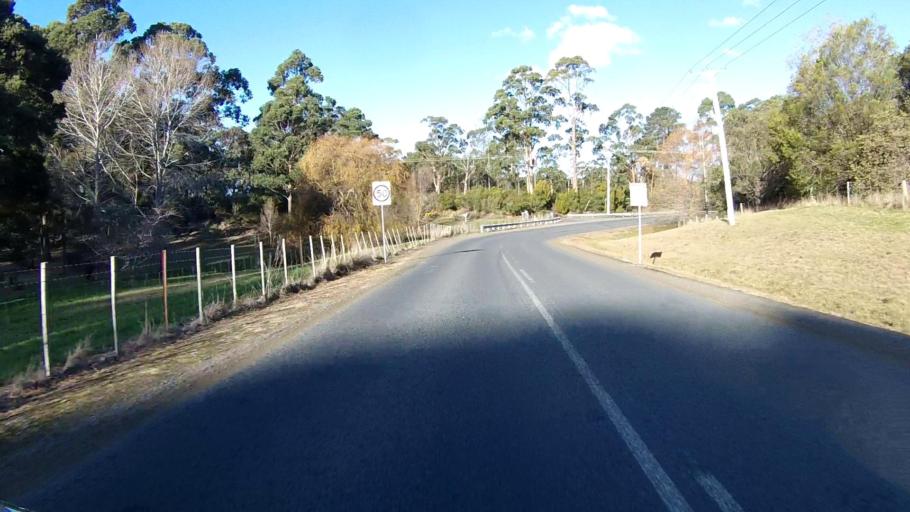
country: AU
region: Tasmania
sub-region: Clarence
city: Sandford
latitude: -43.1511
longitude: 147.8448
